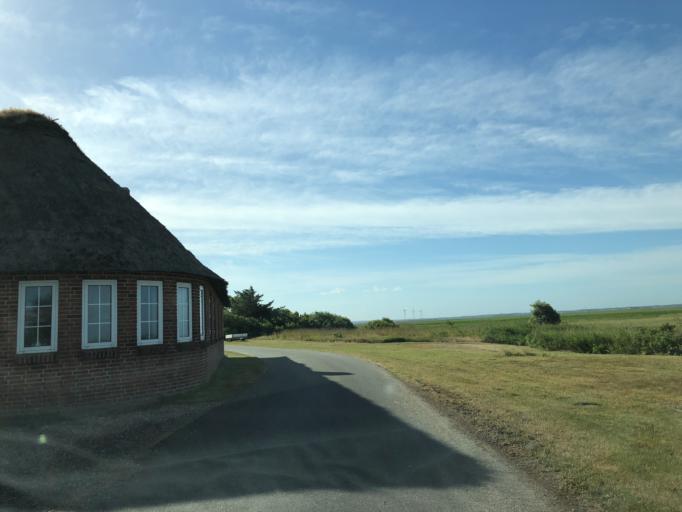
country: DK
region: Central Jutland
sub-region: Holstebro Kommune
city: Ulfborg
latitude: 56.3355
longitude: 8.2617
